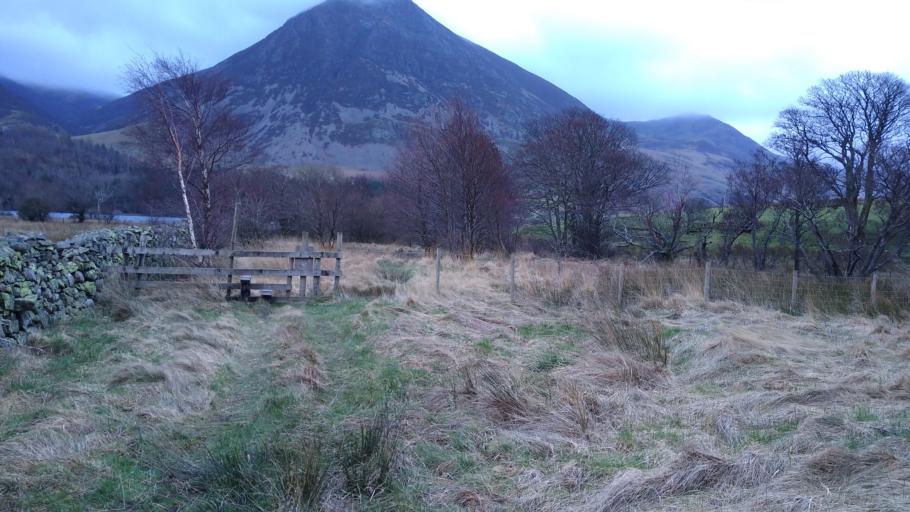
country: GB
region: England
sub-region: Cumbria
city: Cockermouth
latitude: 54.5714
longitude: -3.3173
